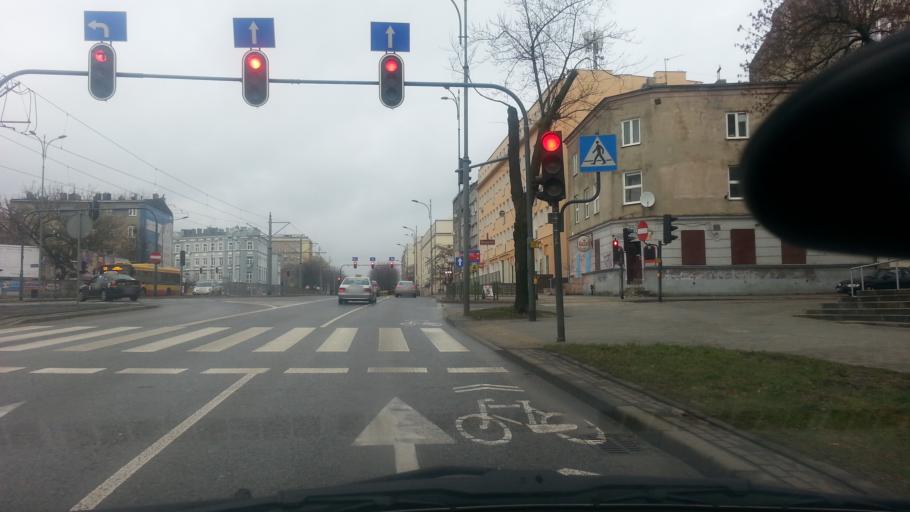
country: PL
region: Lodz Voivodeship
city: Lodz
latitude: 51.7816
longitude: 19.4510
